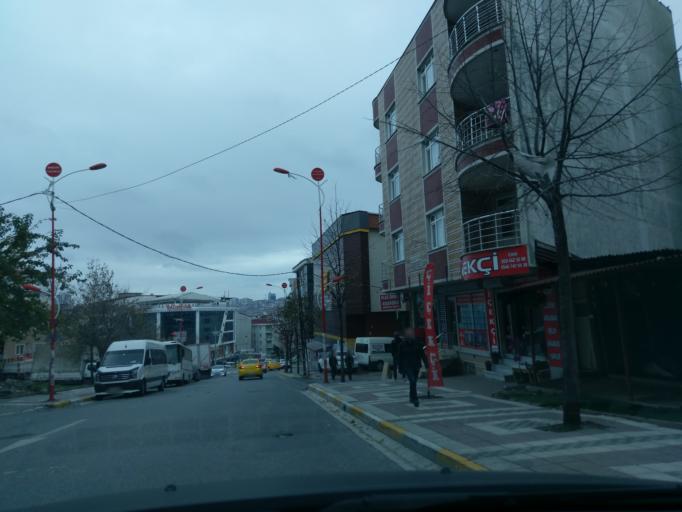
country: TR
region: Istanbul
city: Esenyurt
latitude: 41.0173
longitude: 28.6645
